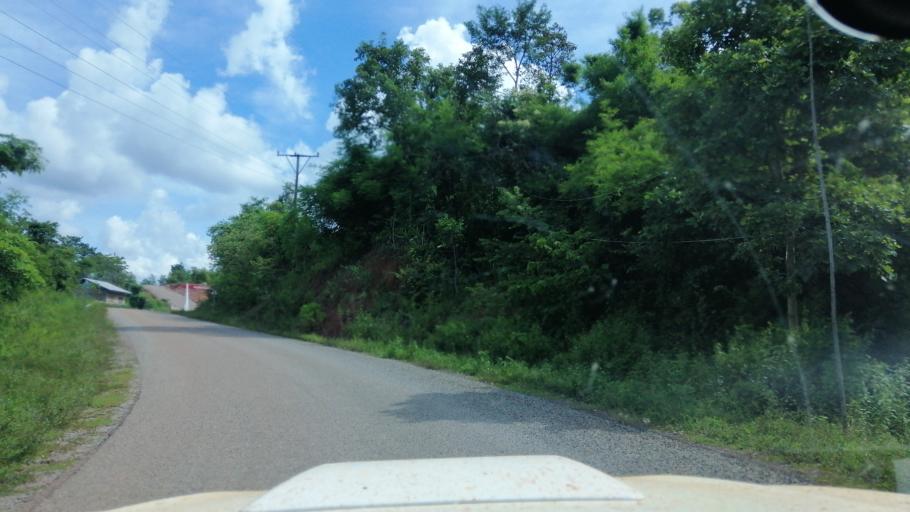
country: TH
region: Nan
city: Mae Charim
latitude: 18.3846
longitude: 101.1546
